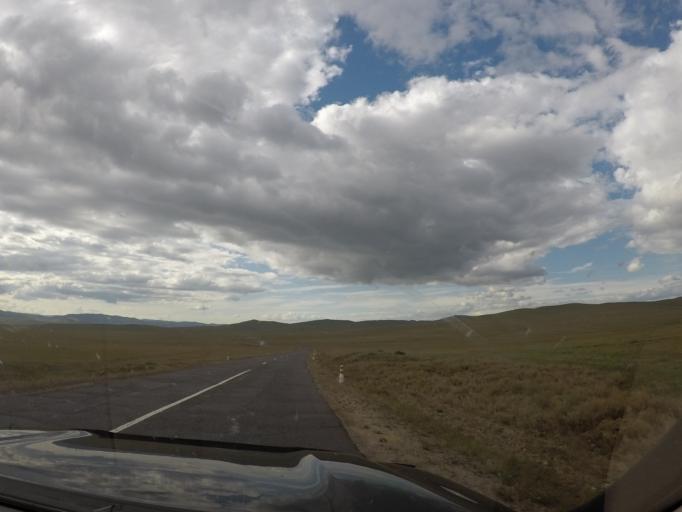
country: MN
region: Hentiy
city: Modot
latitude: 47.5926
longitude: 109.2566
